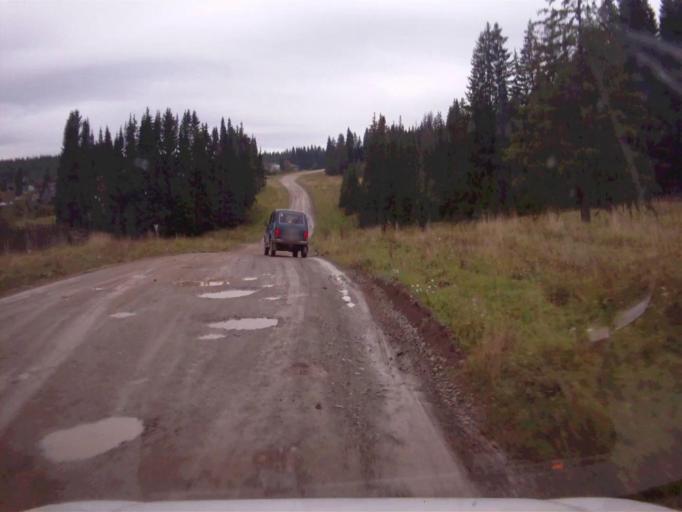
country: RU
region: Chelyabinsk
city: Nyazepetrovsk
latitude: 56.0634
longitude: 59.5665
